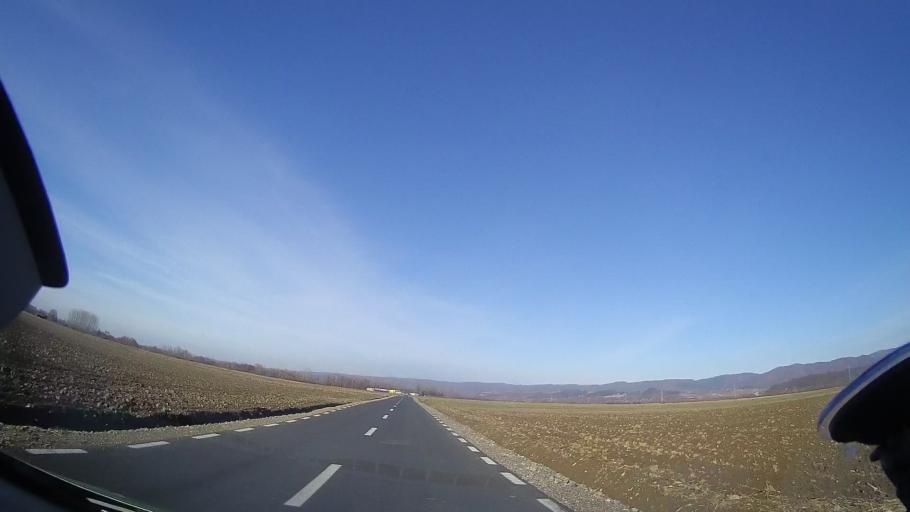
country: RO
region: Bihor
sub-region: Comuna Vadu Crisului
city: Vadu Crisului
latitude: 46.9954
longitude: 22.5068
